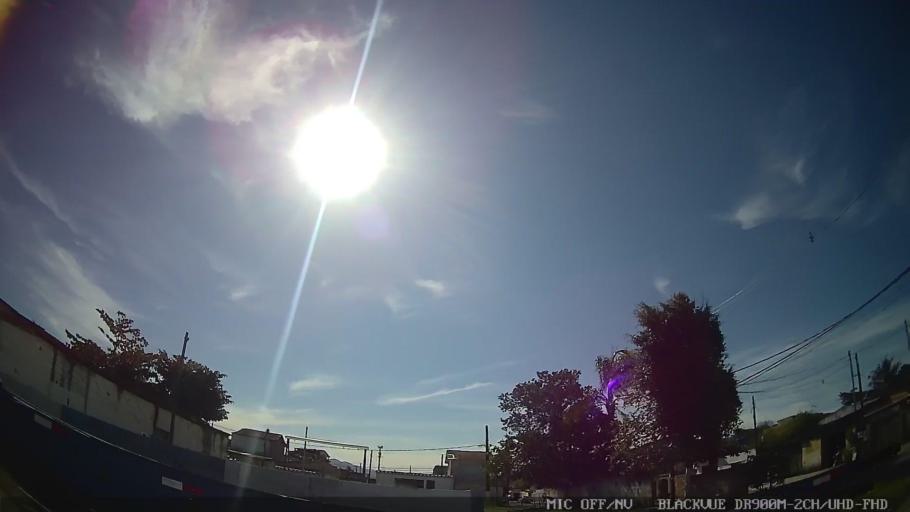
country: BR
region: Sao Paulo
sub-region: Santos
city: Santos
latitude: -23.9408
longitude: -46.2818
